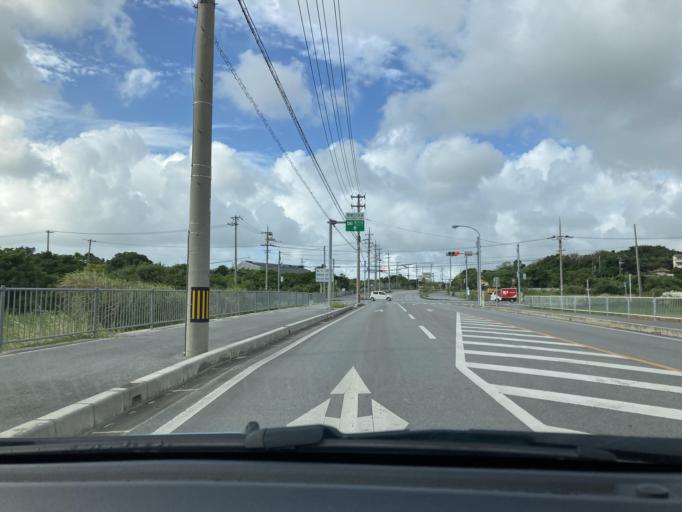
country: JP
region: Okinawa
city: Itoman
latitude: 26.1173
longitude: 127.6918
